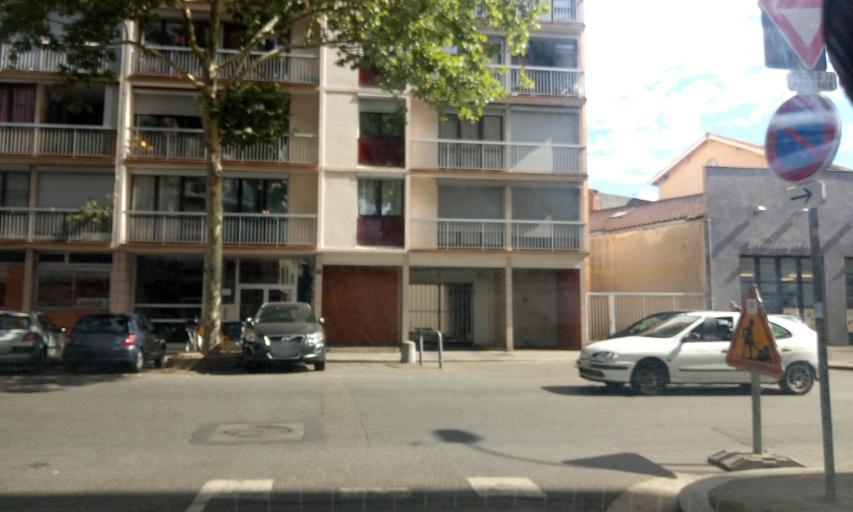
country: FR
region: Rhone-Alpes
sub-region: Departement du Rhone
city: Villeurbanne
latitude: 45.7549
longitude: 4.8805
